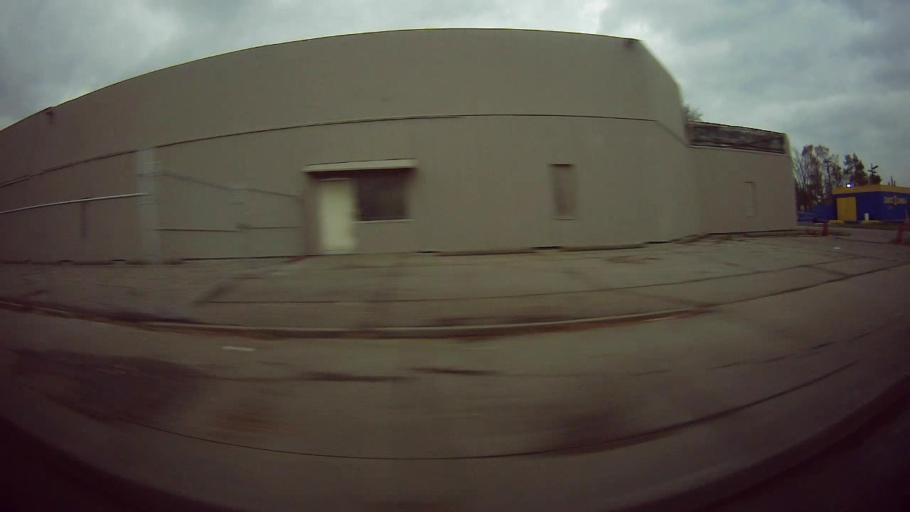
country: US
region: Michigan
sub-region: Wayne County
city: Grosse Pointe Park
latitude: 42.3981
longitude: -82.9903
